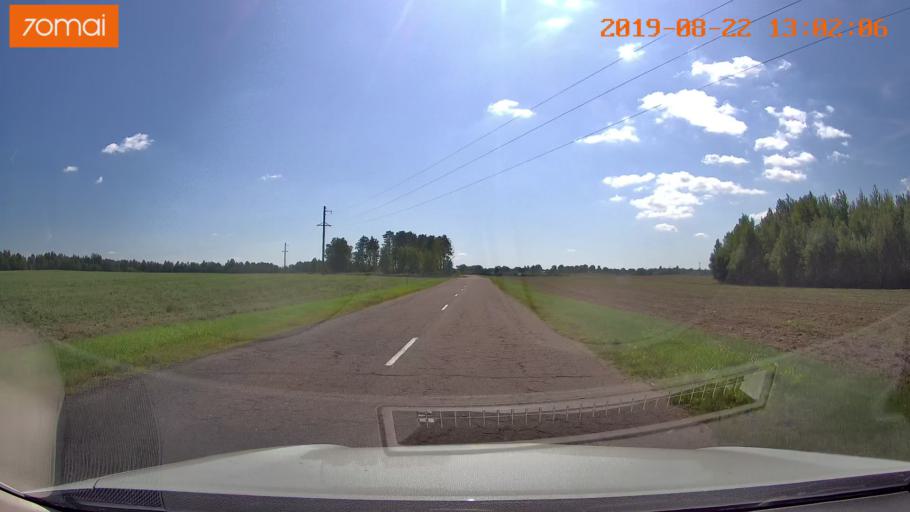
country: BY
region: Minsk
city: Prawdzinski
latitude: 53.3930
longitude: 27.8237
